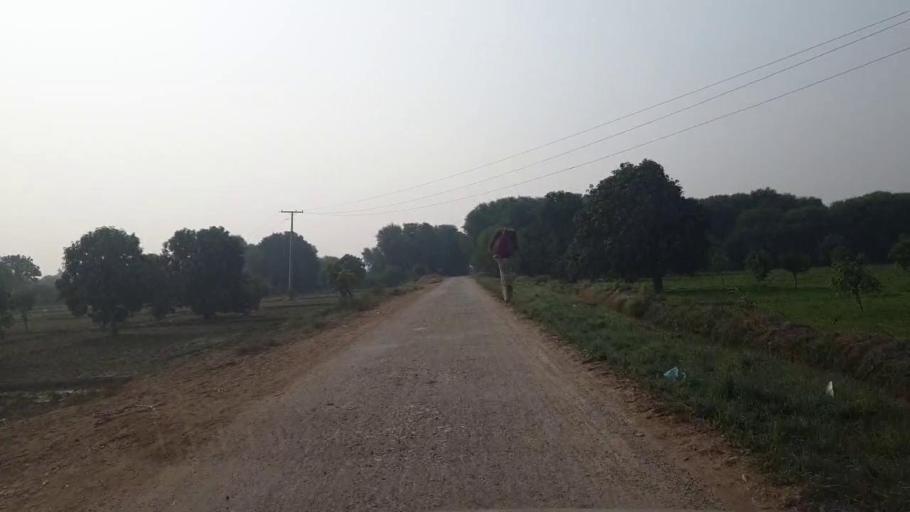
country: PK
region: Sindh
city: Tando Jam
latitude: 25.3247
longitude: 68.5181
